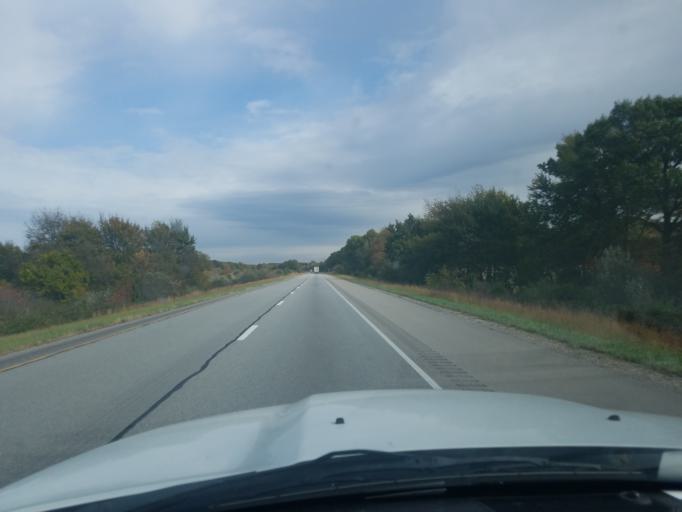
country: US
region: Indiana
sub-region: Warrick County
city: Chandler
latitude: 38.1834
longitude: -87.3835
